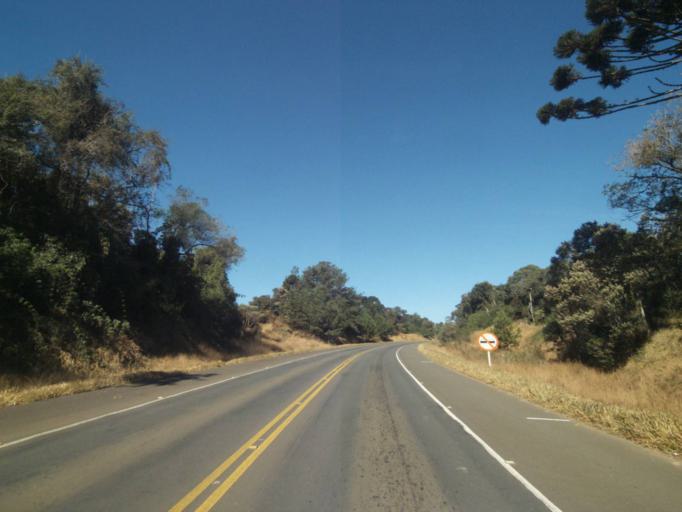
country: BR
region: Parana
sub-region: Tibagi
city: Tibagi
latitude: -24.6636
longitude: -50.4515
